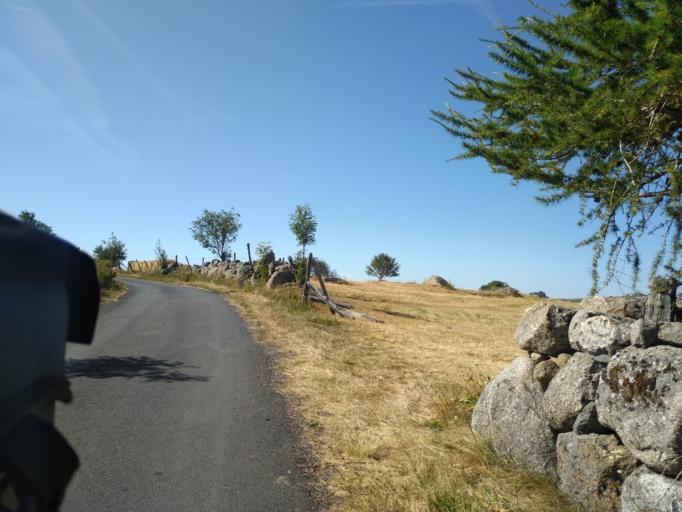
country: FR
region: Languedoc-Roussillon
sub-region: Departement de la Lozere
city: Aumont-Aubrac
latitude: 44.6703
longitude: 3.1024
